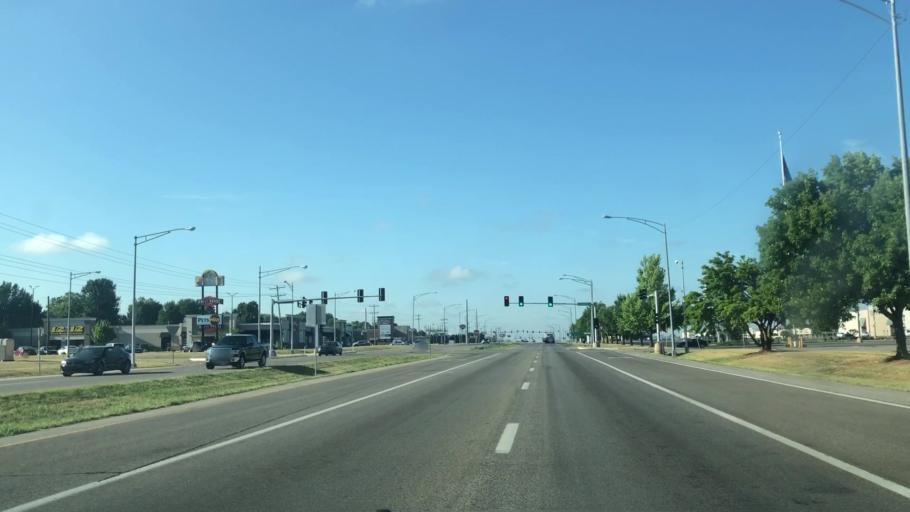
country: US
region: Missouri
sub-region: Greene County
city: Springfield
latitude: 37.1638
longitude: -93.2628
